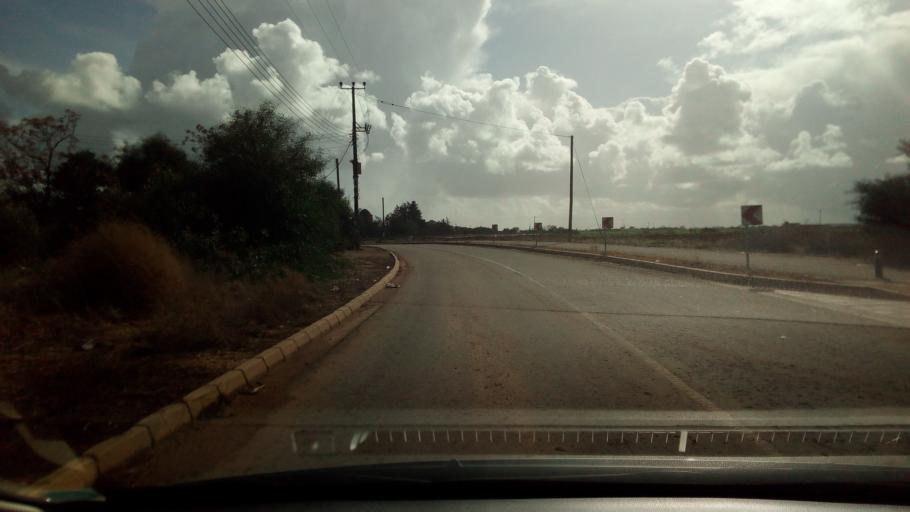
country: CY
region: Ammochostos
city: Avgorou
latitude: 35.0488
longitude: 33.8148
